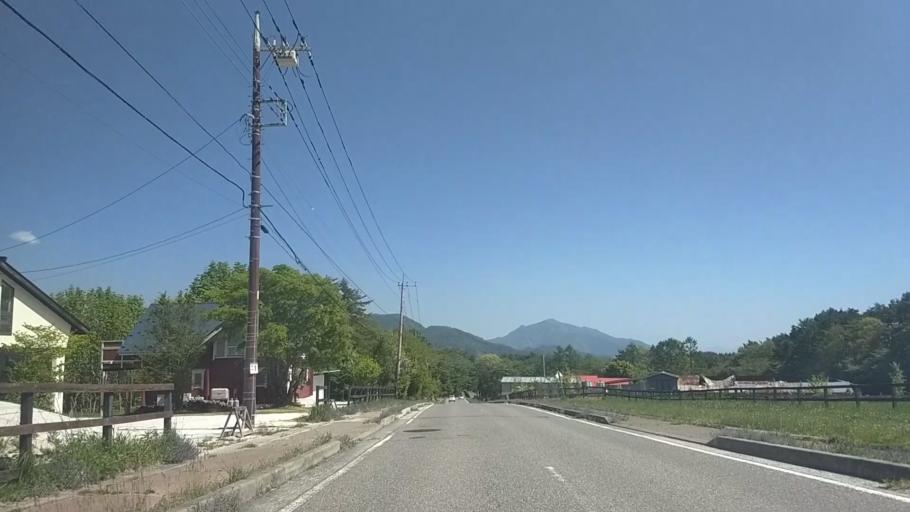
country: JP
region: Yamanashi
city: Nirasaki
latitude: 35.9073
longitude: 138.4324
